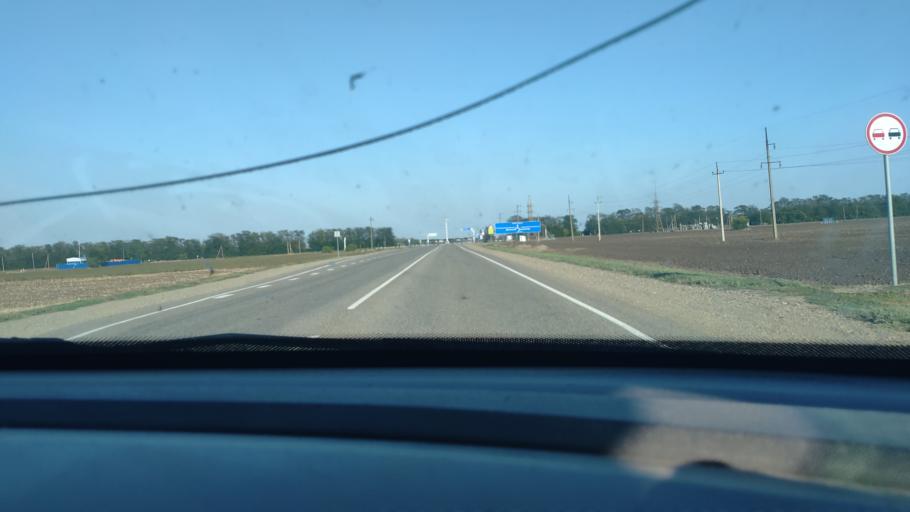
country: RU
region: Krasnodarskiy
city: Staroshcherbinovskaya
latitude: 46.6105
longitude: 38.6497
